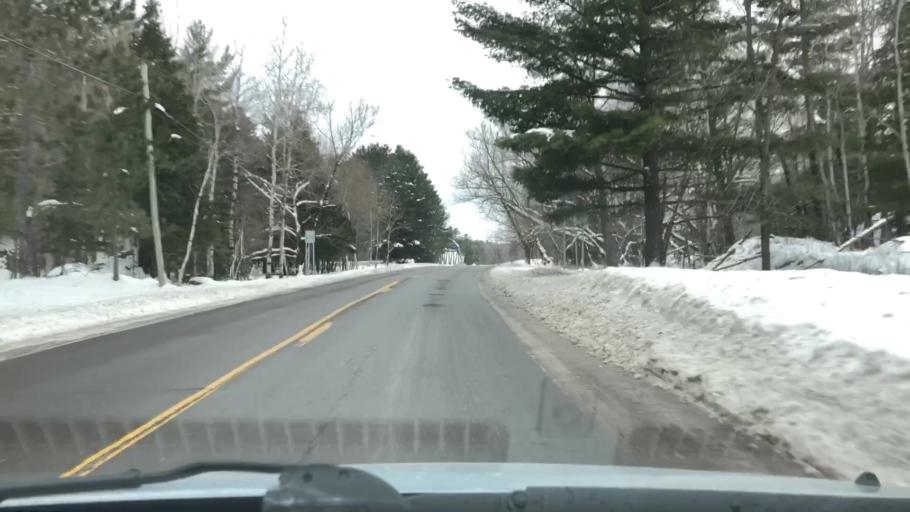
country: US
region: Minnesota
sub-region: Carlton County
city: Carlton
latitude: 46.6645
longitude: -92.4008
